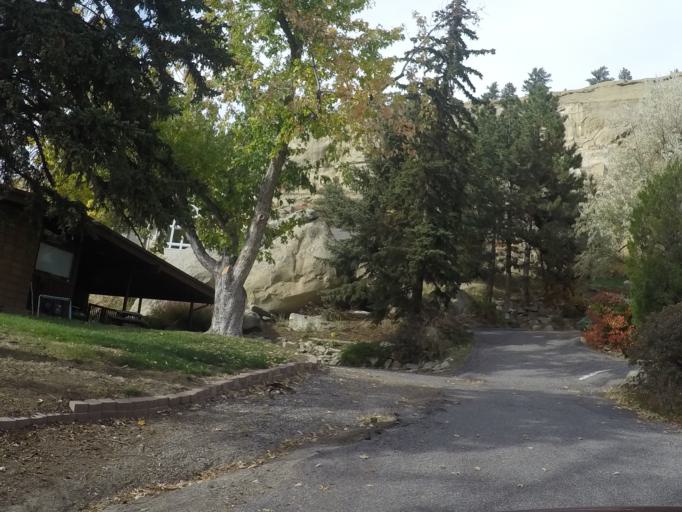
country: US
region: Montana
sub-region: Yellowstone County
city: Billings
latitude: 45.8012
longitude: -108.5552
